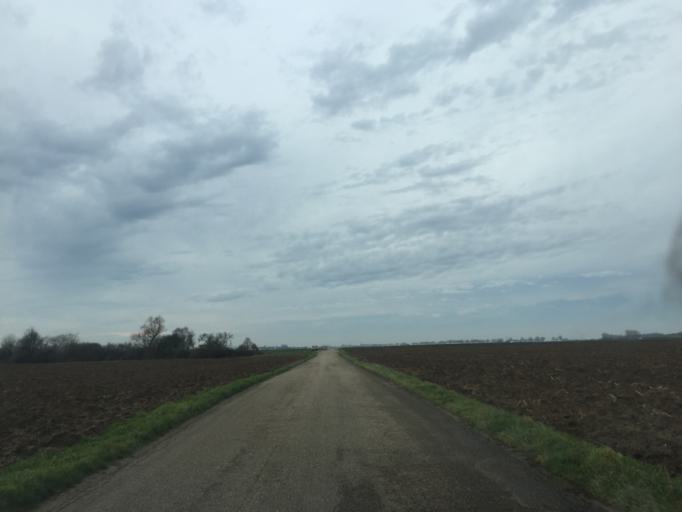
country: FR
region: Franche-Comte
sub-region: Departement du Jura
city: Tavaux
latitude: 47.0299
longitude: 5.4157
